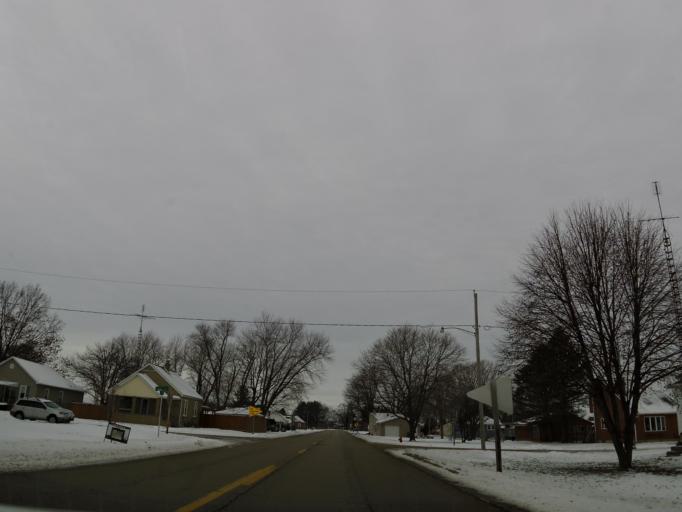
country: US
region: Illinois
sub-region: LaSalle County
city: Peru
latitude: 41.2622
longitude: -89.1242
